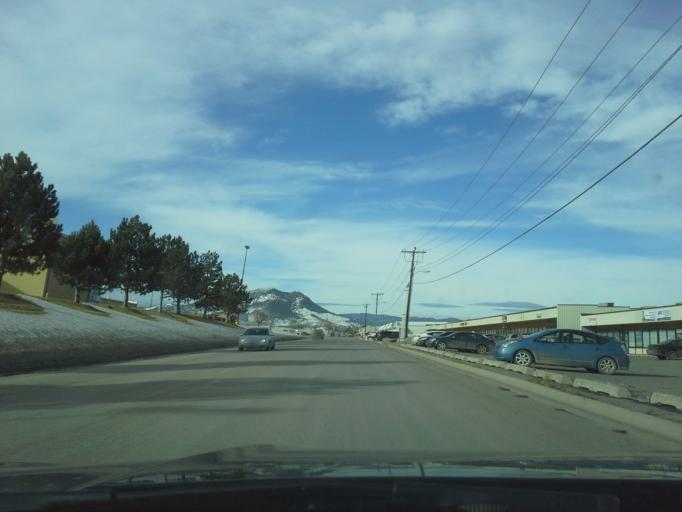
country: US
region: Montana
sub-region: Lewis and Clark County
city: Helena
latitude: 46.5944
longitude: -111.9894
